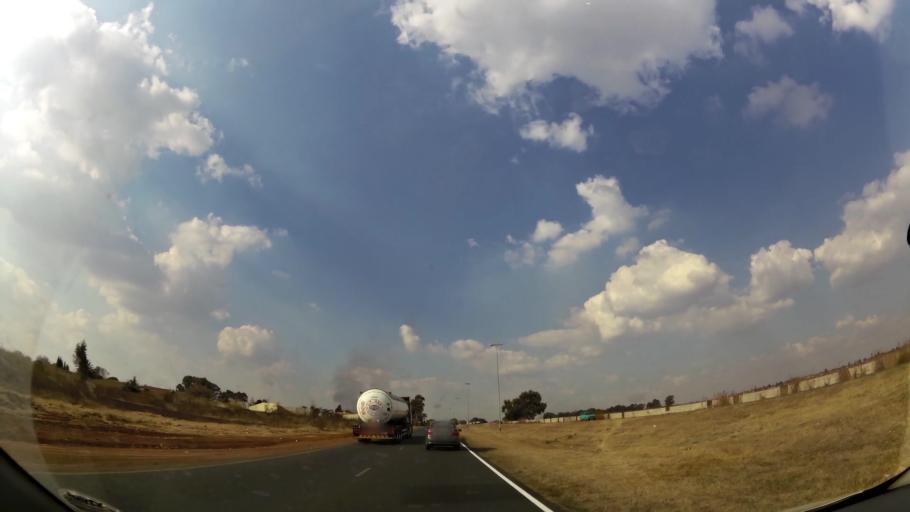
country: ZA
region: Gauteng
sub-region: Ekurhuleni Metropolitan Municipality
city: Germiston
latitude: -26.2890
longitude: 28.2330
